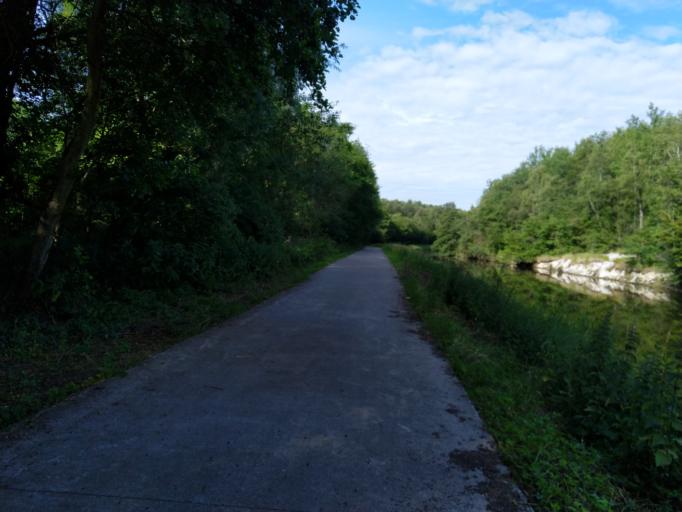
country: FR
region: Nord-Pas-de-Calais
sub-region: Departement du Nord
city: Recquignies
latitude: 50.2800
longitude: 4.0305
